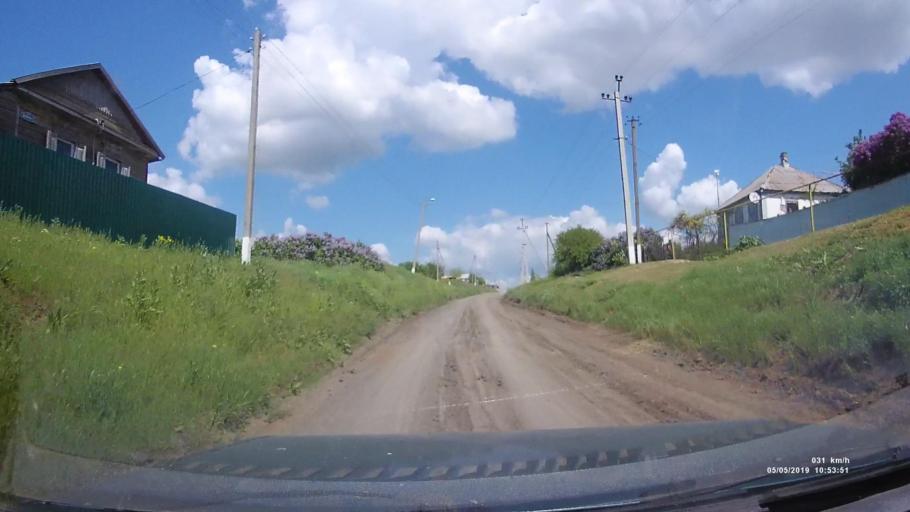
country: RU
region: Rostov
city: Ust'-Donetskiy
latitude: 47.6556
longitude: 40.8239
